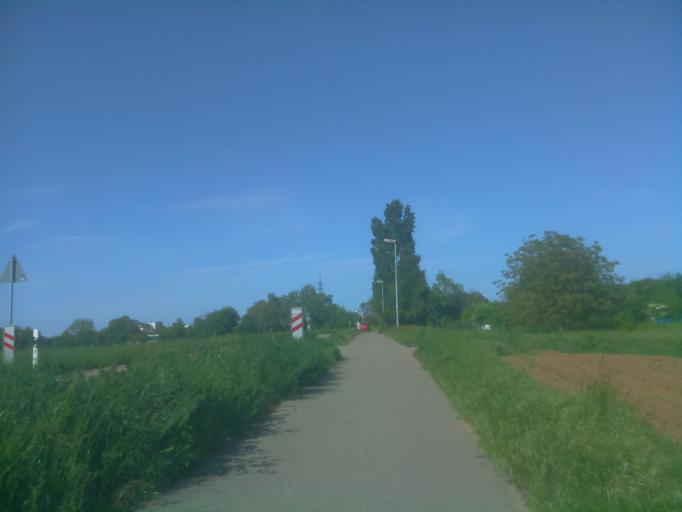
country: DE
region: Baden-Wuerttemberg
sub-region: Karlsruhe Region
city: Schwetzingen
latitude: 49.3944
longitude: 8.5739
